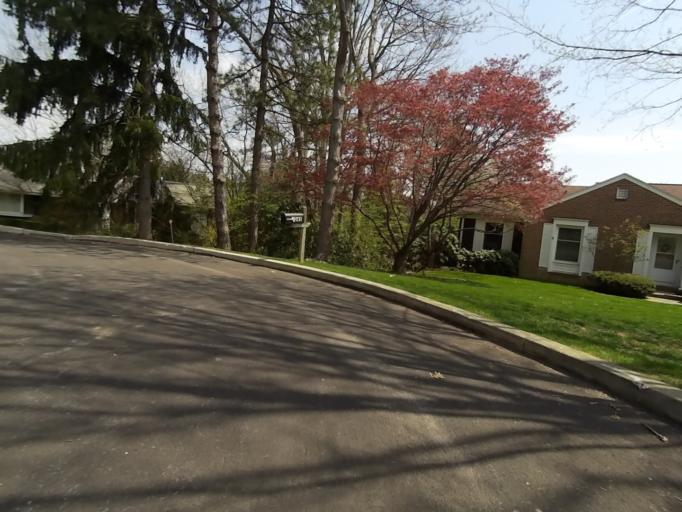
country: US
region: Pennsylvania
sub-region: Centre County
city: Park Forest Village
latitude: 40.7964
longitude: -77.9012
